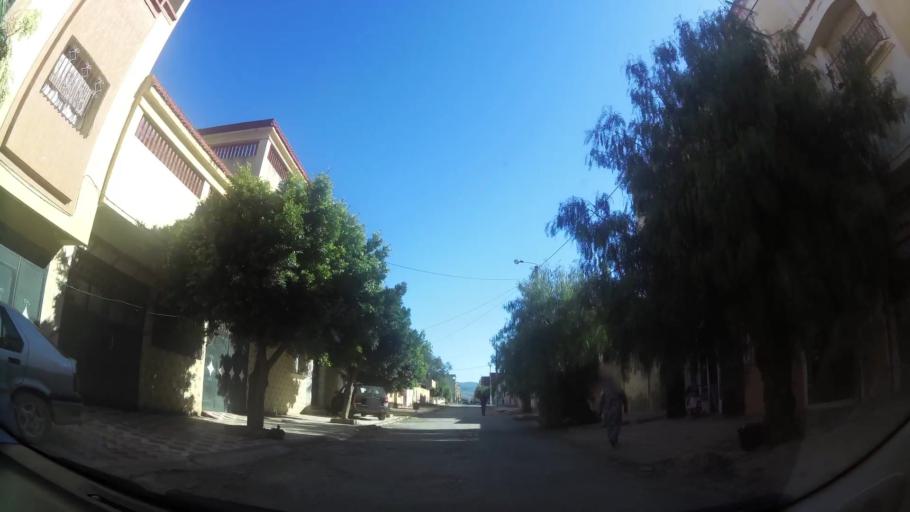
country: MA
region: Oriental
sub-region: Berkane-Taourirt
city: Ahfir
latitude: 34.9561
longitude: -2.0993
